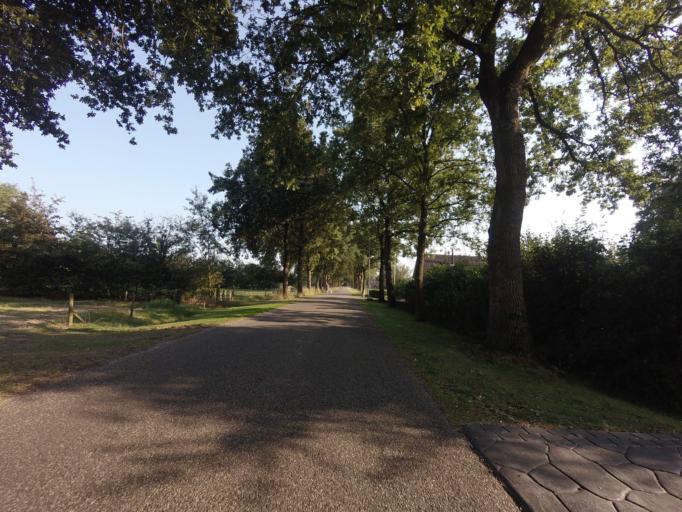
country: NL
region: Drenthe
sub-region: Gemeente Tynaarlo
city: Vries
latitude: 53.1356
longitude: 6.4894
